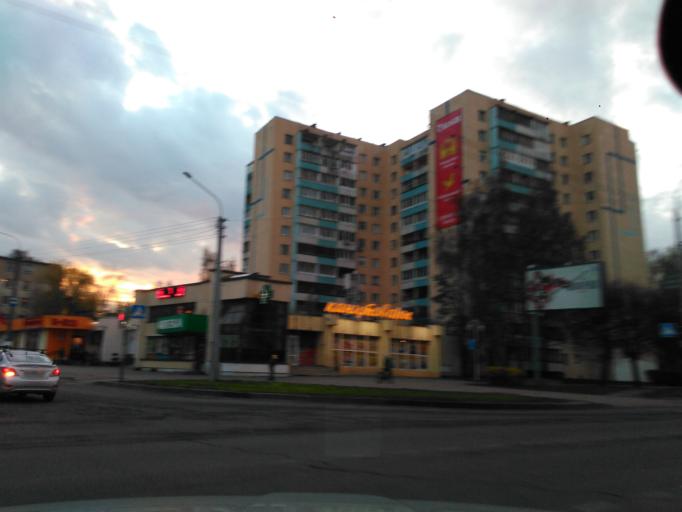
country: BY
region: Minsk
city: Novoye Medvezhino
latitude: 53.9157
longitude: 27.4948
